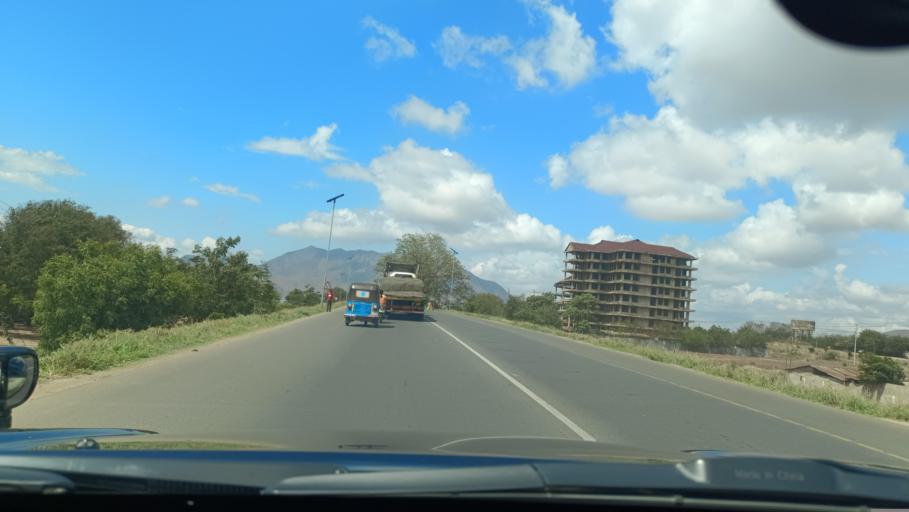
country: TZ
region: Morogoro
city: Morogoro
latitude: -6.8061
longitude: 37.6578
